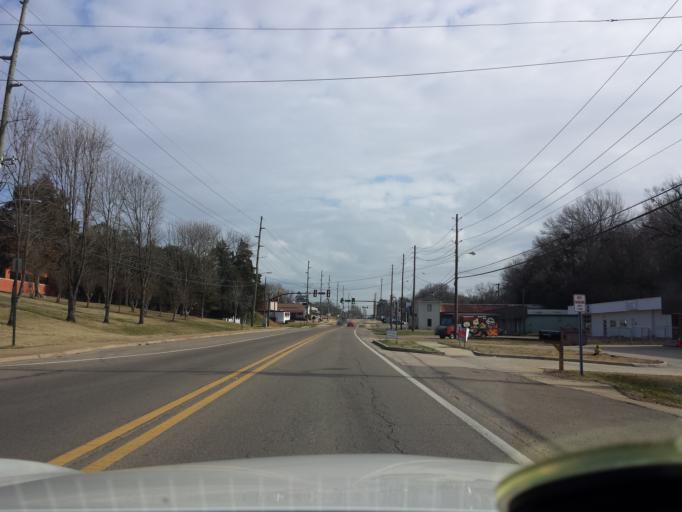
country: US
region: Mississippi
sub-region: Oktibbeha County
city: Starkville
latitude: 33.4659
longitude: -88.8202
